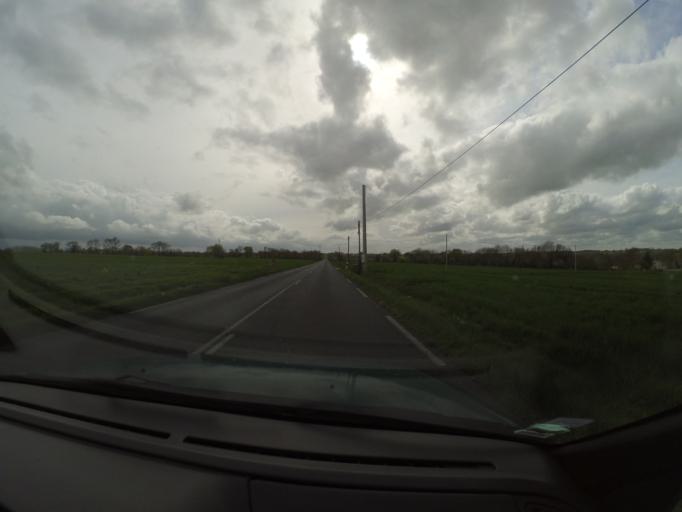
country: FR
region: Pays de la Loire
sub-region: Departement de Maine-et-Loire
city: Saint-Laurent-des-Autels
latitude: 47.2961
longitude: -1.1717
